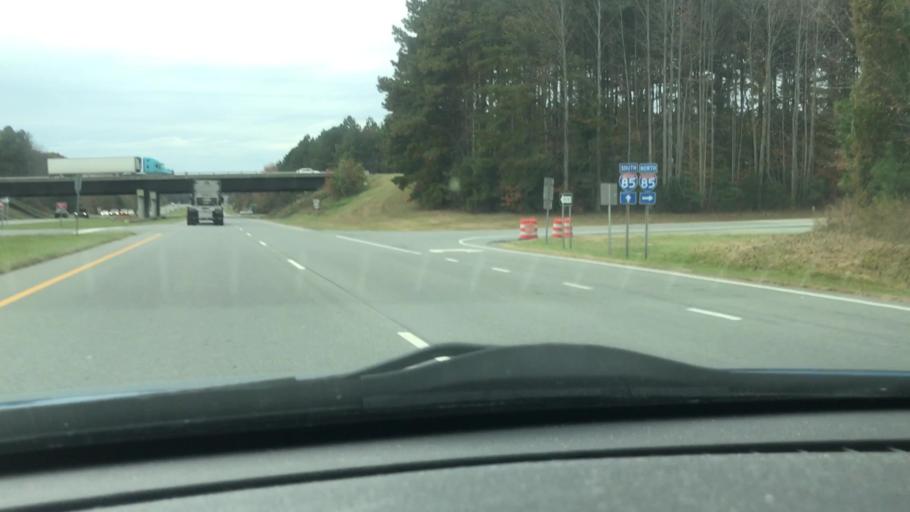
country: US
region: North Carolina
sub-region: Davidson County
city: Lexington
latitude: 35.8092
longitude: -80.1803
